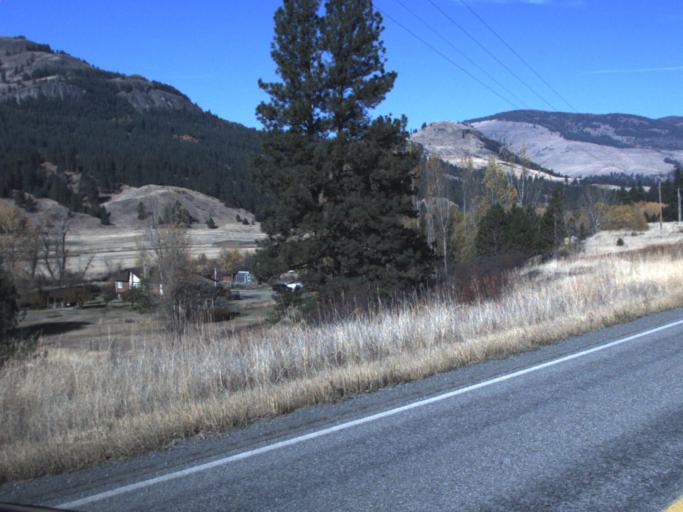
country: US
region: Washington
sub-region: Ferry County
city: Republic
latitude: 48.8415
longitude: -118.5955
